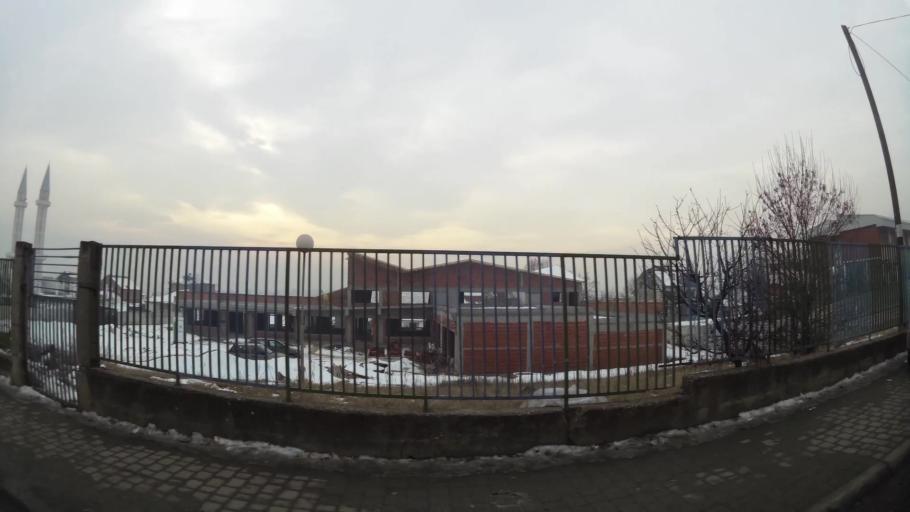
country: MK
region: Suto Orizari
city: Suto Orizare
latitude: 42.0381
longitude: 21.4253
